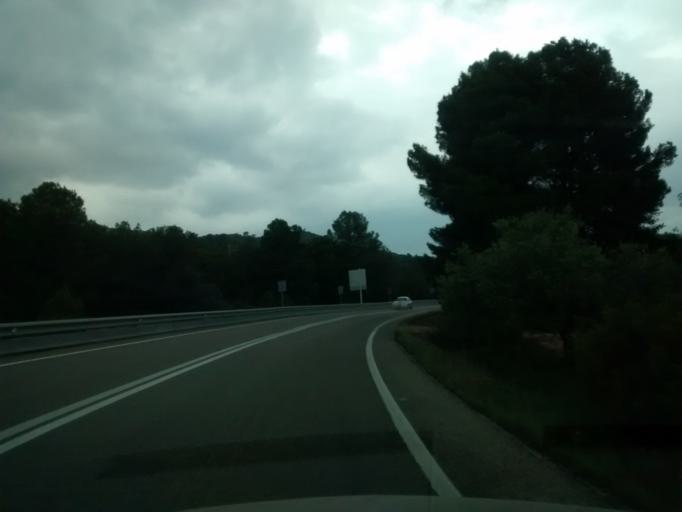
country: ES
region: Catalonia
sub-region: Provincia de Tarragona
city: Benifallet
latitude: 41.0228
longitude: 0.4986
